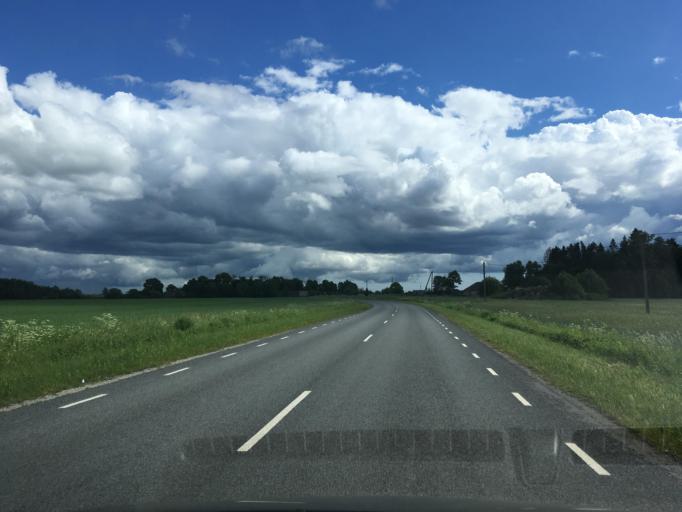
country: EE
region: Paernumaa
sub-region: Halinga vald
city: Parnu-Jaagupi
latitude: 58.6188
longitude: 24.4527
